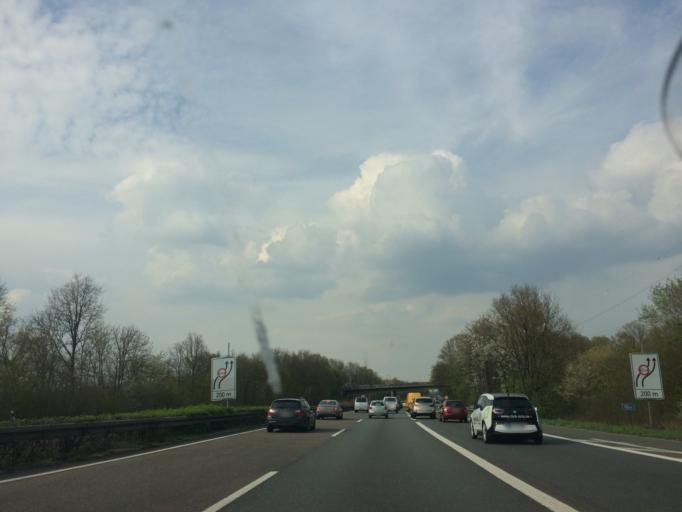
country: DE
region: North Rhine-Westphalia
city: Witten
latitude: 51.5018
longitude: 7.3862
